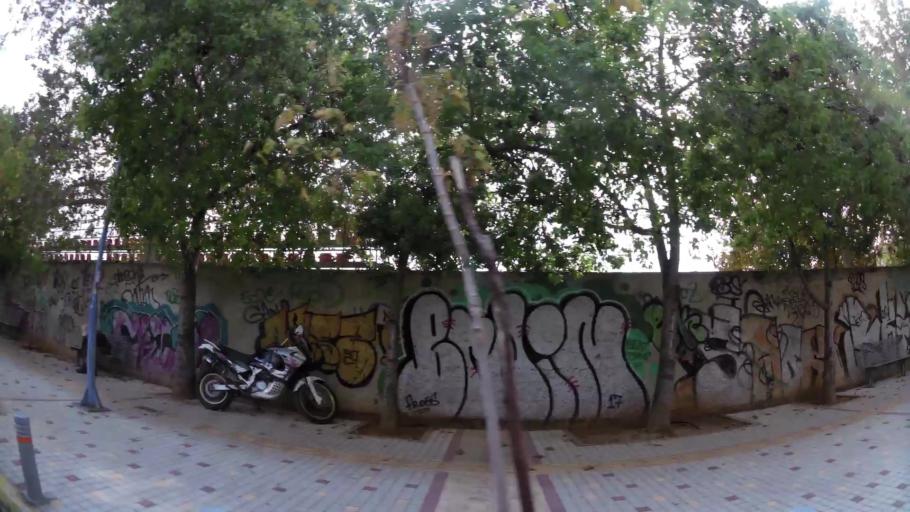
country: GR
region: Attica
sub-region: Nomarchia Athinas
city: Moskhaton
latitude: 37.9538
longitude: 23.6861
